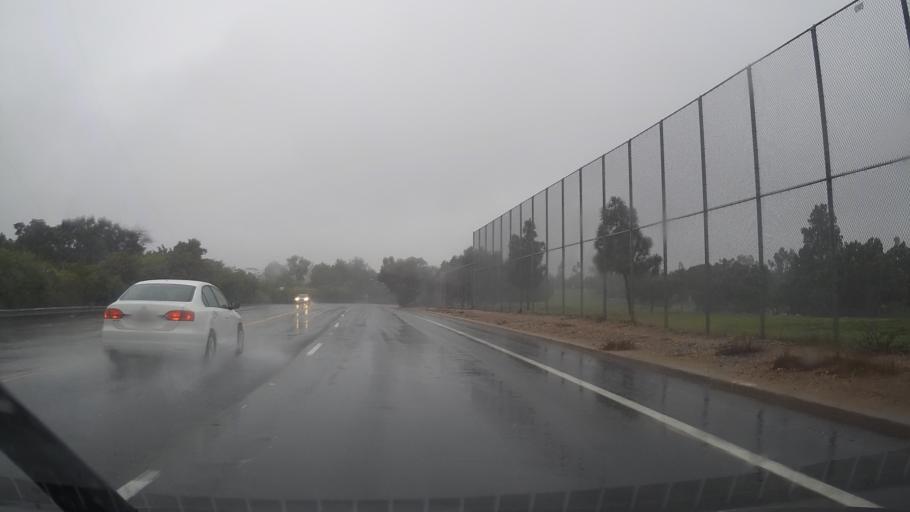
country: US
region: California
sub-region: San Diego County
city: San Diego
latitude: 32.7330
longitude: -117.1368
